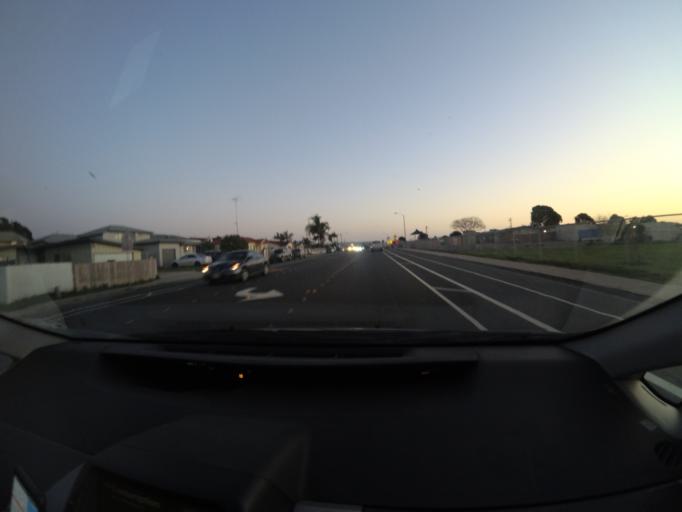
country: US
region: California
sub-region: San Diego County
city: Imperial Beach
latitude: 32.5791
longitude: -117.1057
